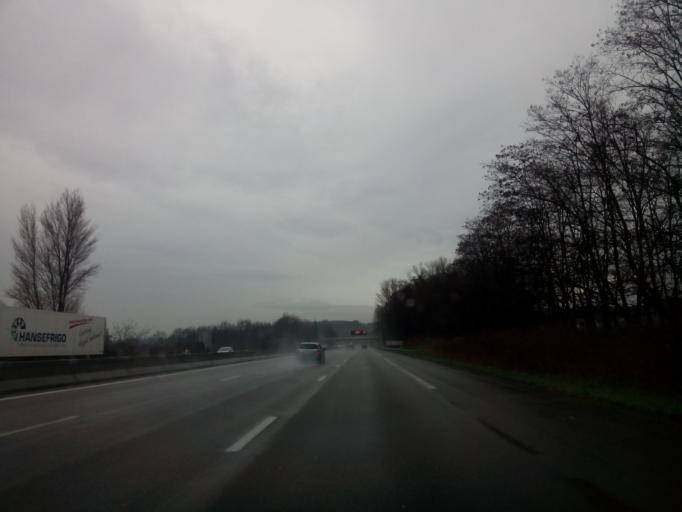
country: FR
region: Rhone-Alpes
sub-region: Departement de la Drome
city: Mercurol
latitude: 45.1072
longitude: 4.8834
